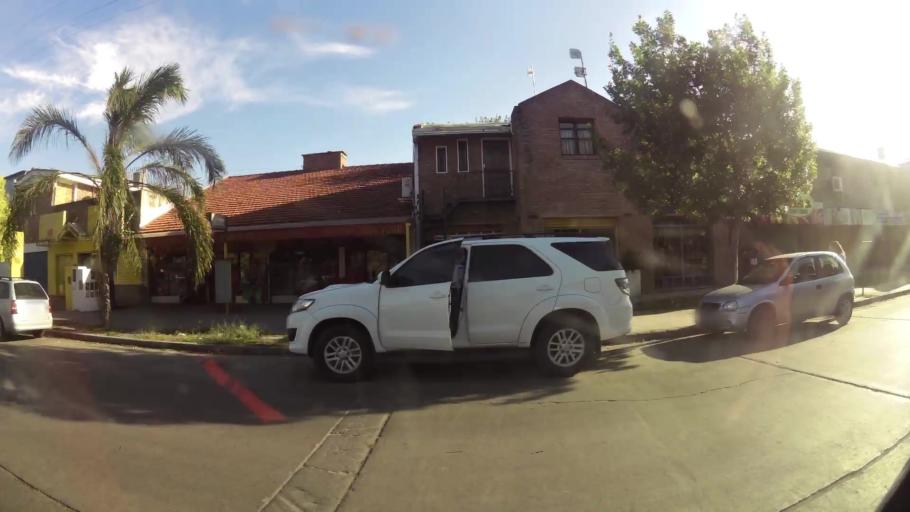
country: AR
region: Cordoba
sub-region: Departamento de Capital
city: Cordoba
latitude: -31.3593
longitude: -64.2239
